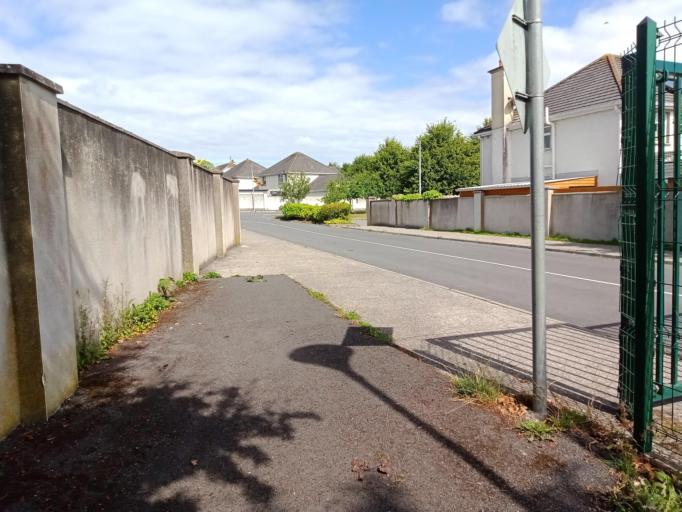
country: IE
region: Leinster
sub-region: Kilkenny
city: Thomastown
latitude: 52.5288
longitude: -7.1374
